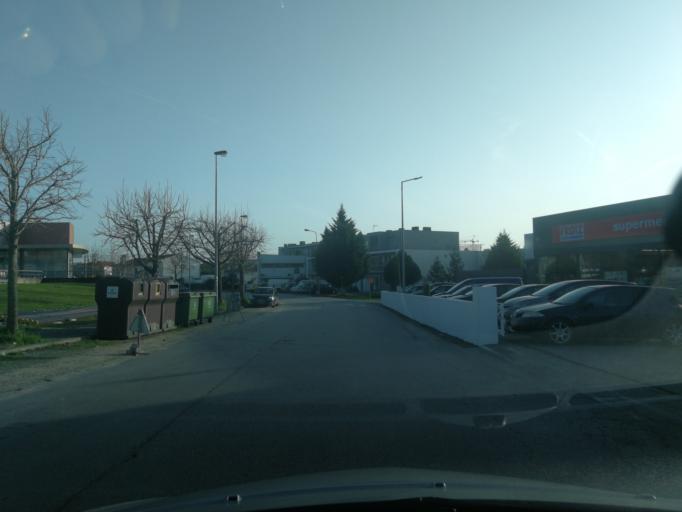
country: PT
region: Braga
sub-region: Barcelos
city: Galegos
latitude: 41.5204
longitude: -8.5723
